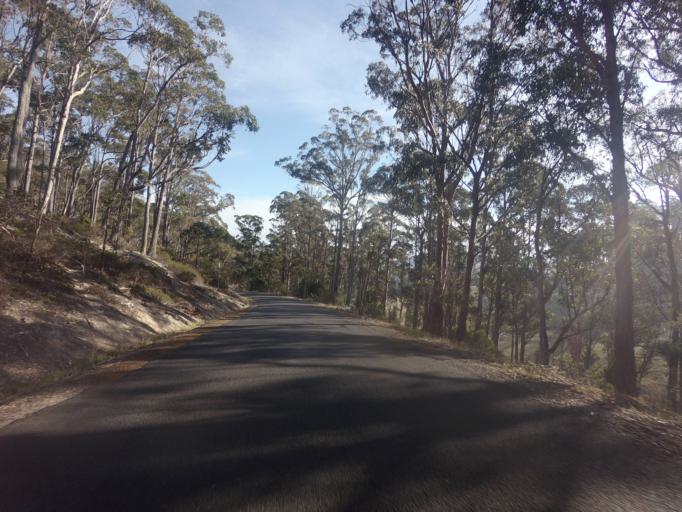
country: AU
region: Tasmania
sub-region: Sorell
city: Sorell
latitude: -42.4842
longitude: 147.4508
